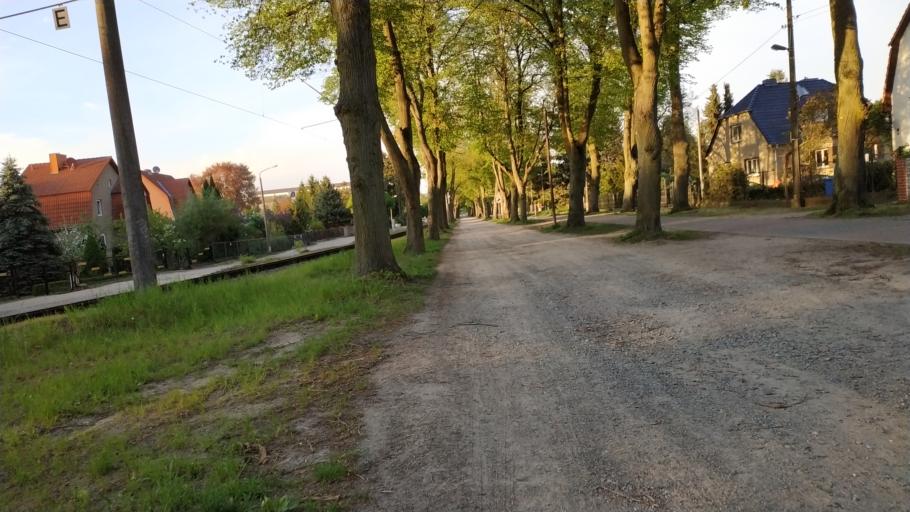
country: DE
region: Brandenburg
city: Petershagen
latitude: 52.5333
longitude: 13.8403
